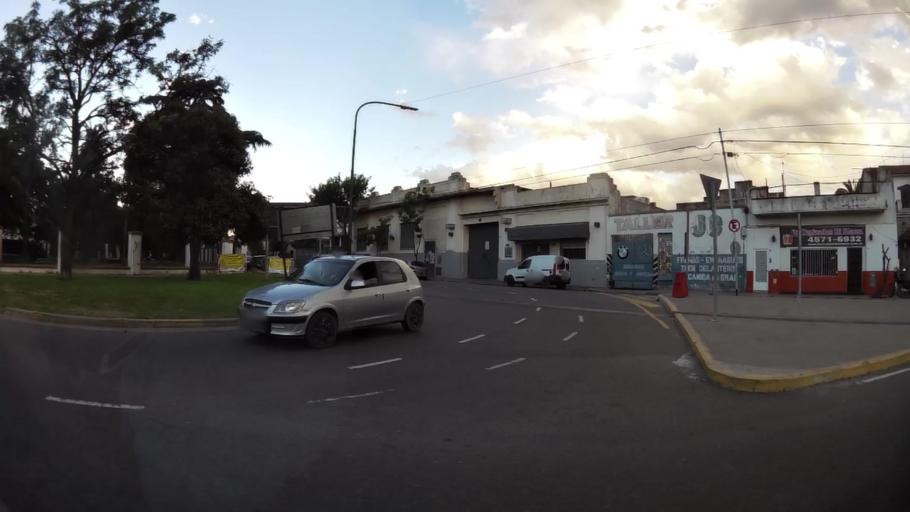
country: AR
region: Buenos Aires
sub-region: Partido de General San Martin
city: General San Martin
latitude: -34.5691
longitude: -58.5085
